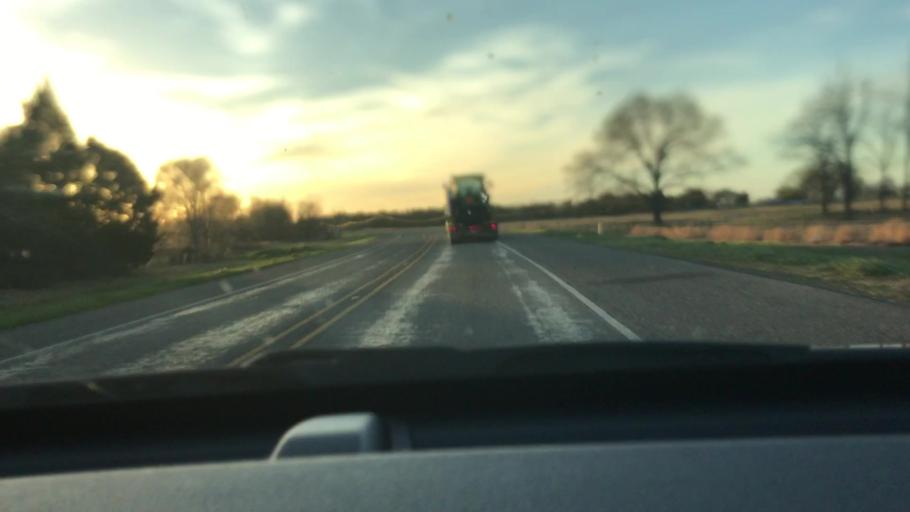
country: US
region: Texas
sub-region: Lamar County
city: Blossom
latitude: 33.6641
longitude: -95.3129
